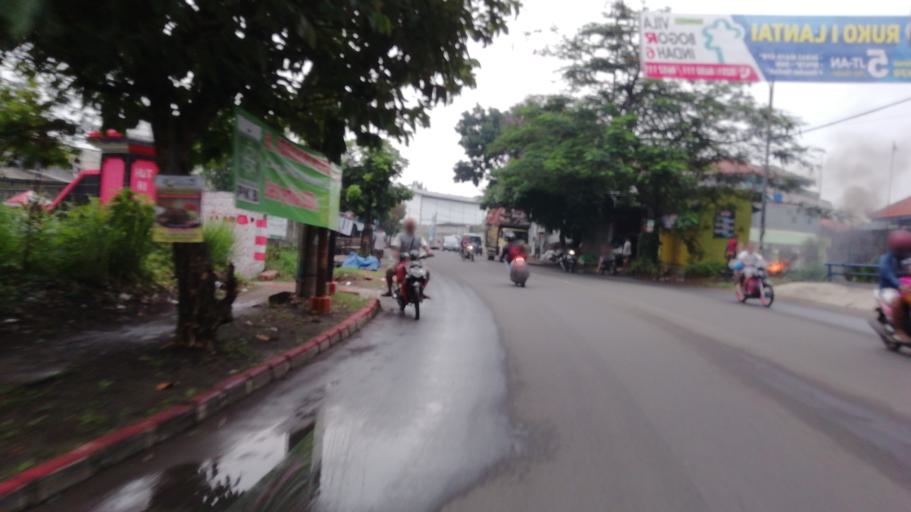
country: ID
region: West Java
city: Cibinong
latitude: -6.5284
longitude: 106.8101
